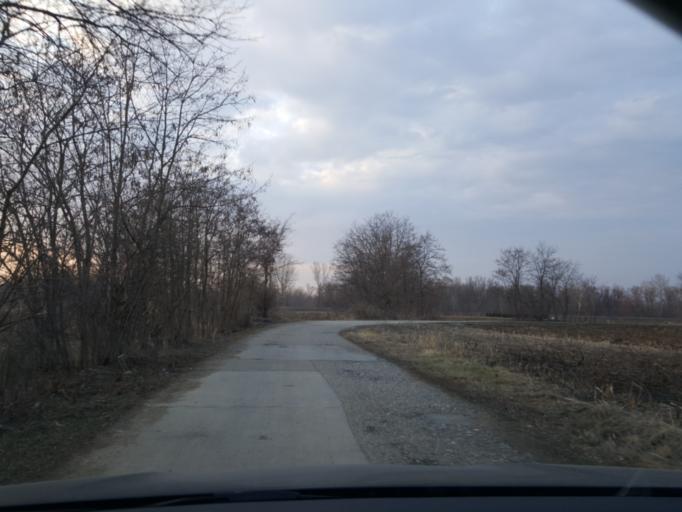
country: RS
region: Central Serbia
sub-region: Nisavski Okrug
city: Aleksinac
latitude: 43.5692
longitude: 21.6420
